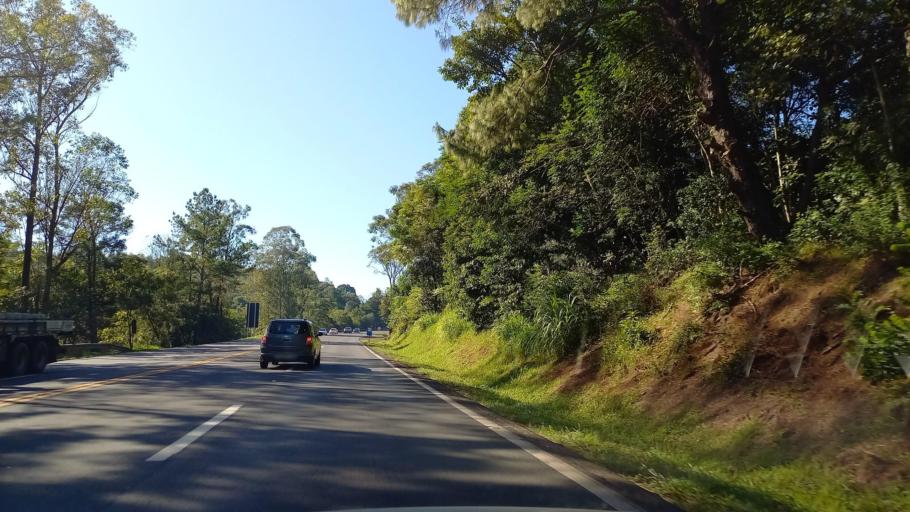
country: BR
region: Rio Grande do Sul
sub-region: Montenegro
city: Montenegro
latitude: -29.8008
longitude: -51.5172
